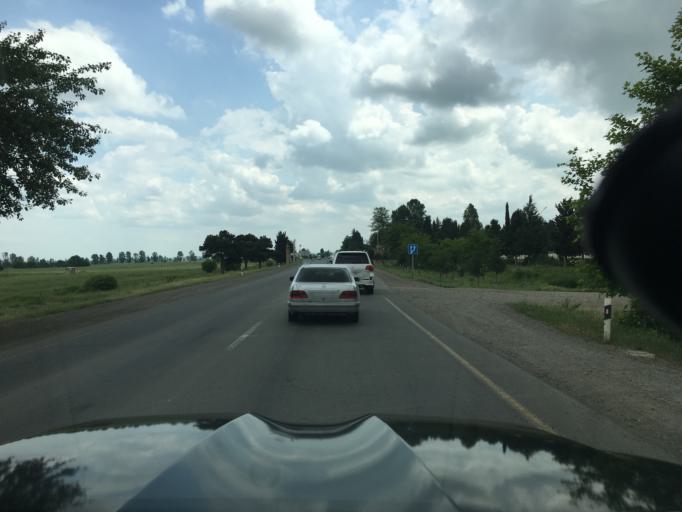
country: AZ
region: Tovuz
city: Tovuz
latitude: 40.9602
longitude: 45.7221
